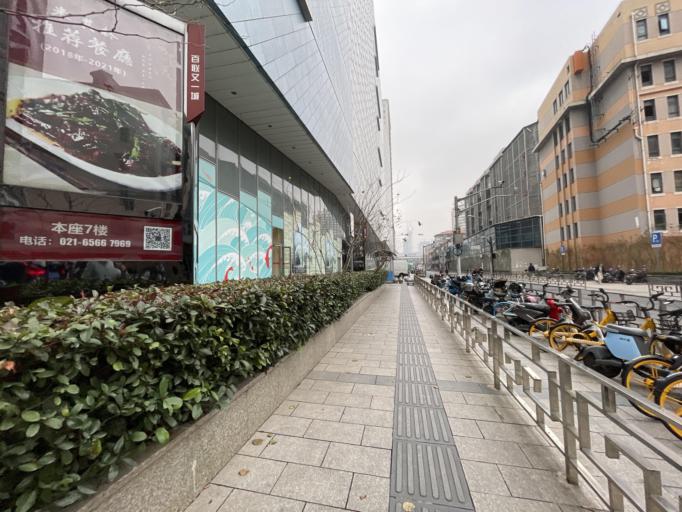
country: CN
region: Shanghai Shi
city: Yangpu
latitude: 31.3036
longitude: 121.5115
